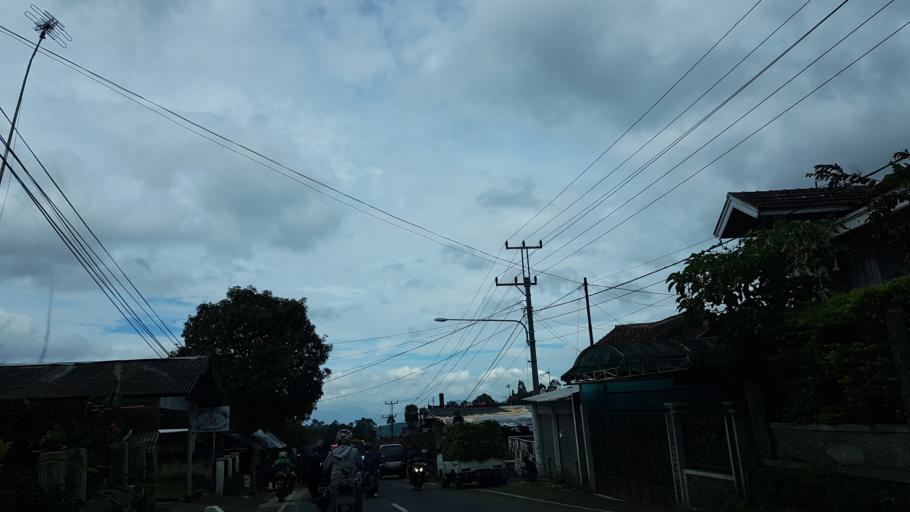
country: ID
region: West Java
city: Banjar
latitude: -7.1133
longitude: 107.4397
